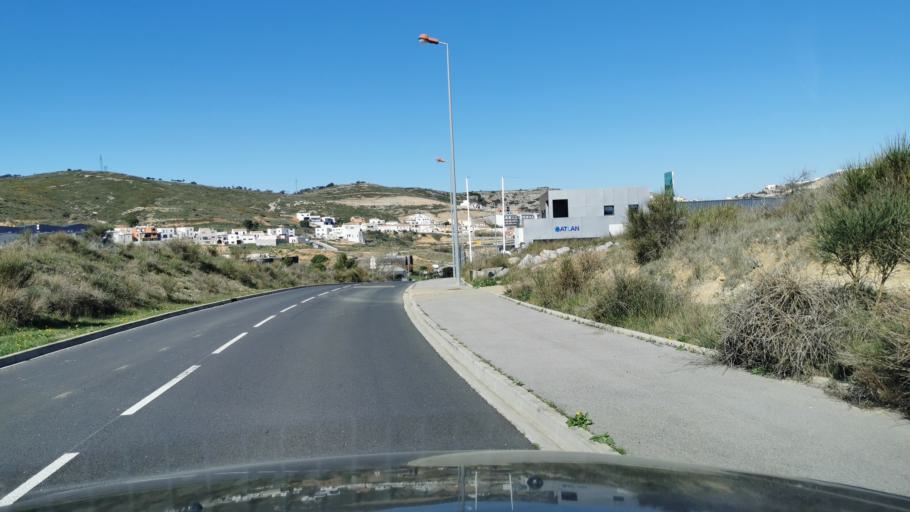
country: FR
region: Languedoc-Roussillon
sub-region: Departement de l'Aude
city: Narbonne
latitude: 43.1541
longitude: 2.9681
